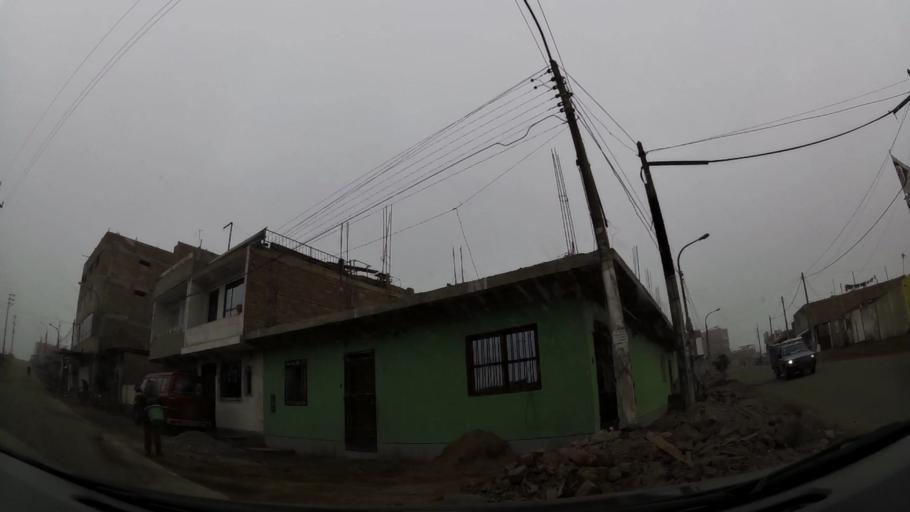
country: PE
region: Lima
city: Ventanilla
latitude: -11.8294
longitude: -77.1043
